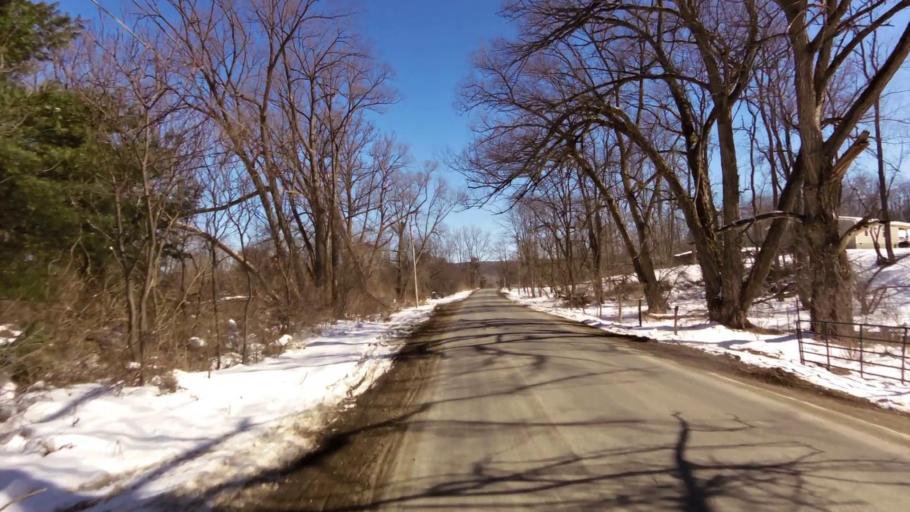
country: US
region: New York
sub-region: Allegany County
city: Houghton
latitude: 42.3637
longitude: -78.1389
